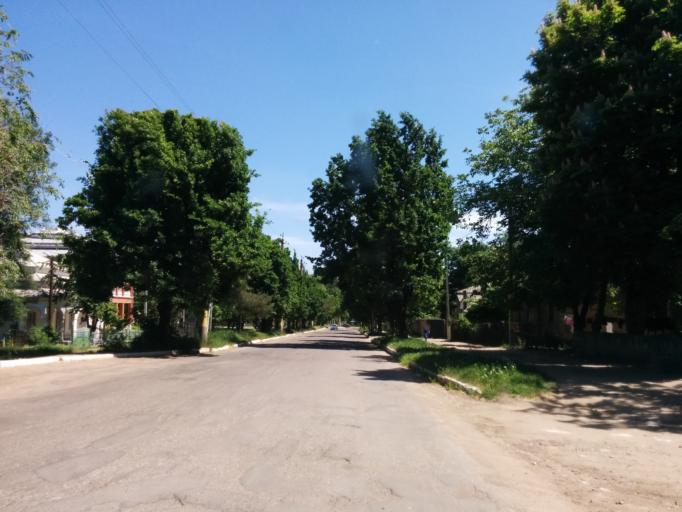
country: MD
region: Raionul Soroca
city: Soroca
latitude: 48.1618
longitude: 28.2874
